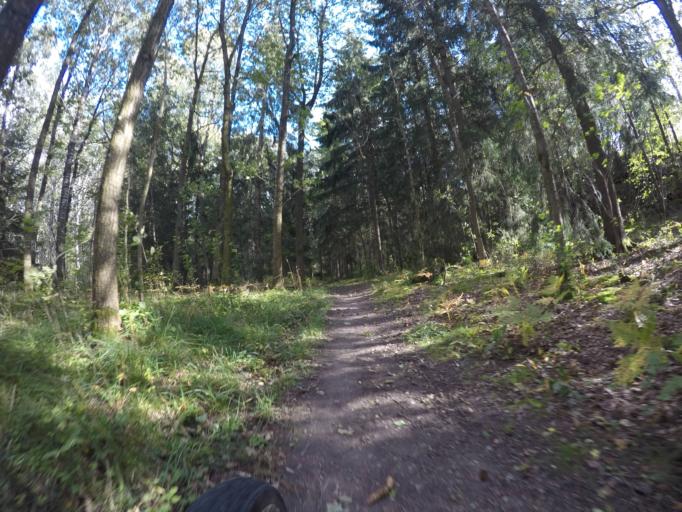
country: SE
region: Vaestmanland
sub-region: Kopings Kommun
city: Koping
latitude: 59.5083
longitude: 16.0210
